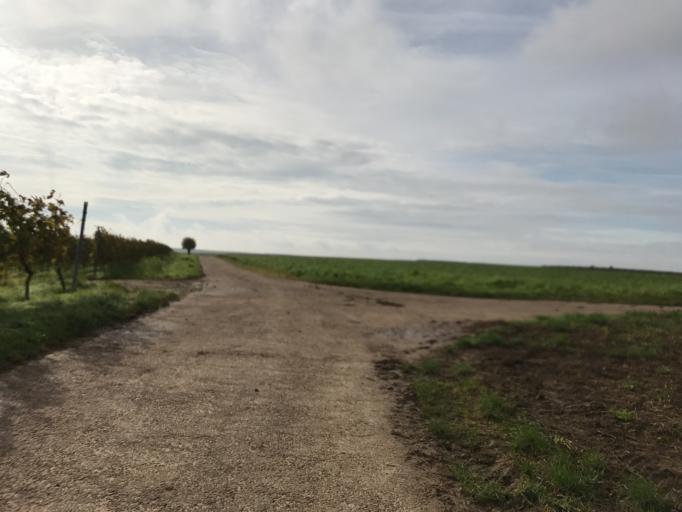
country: DE
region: Rheinland-Pfalz
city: Bubenheim
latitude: 49.9220
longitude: 8.0668
